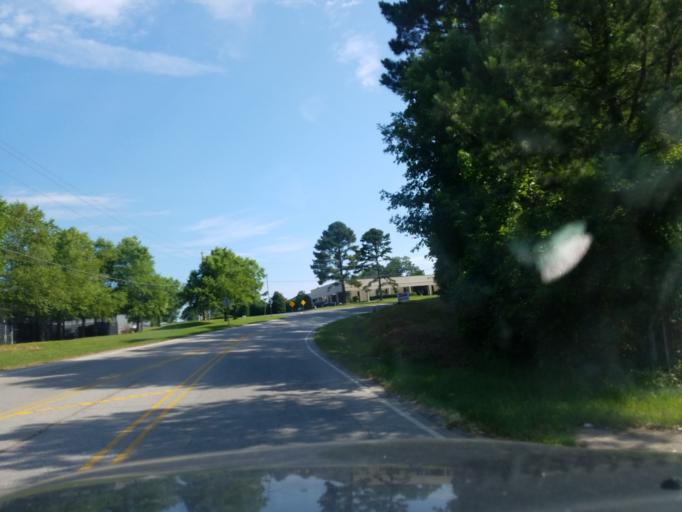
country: US
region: North Carolina
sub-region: Vance County
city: Henderson
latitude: 36.3387
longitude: -78.4379
